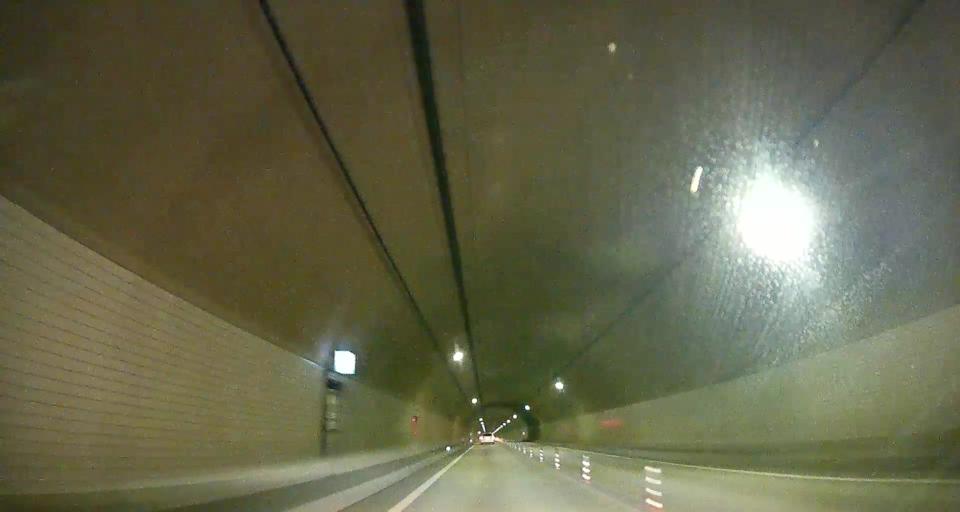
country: JP
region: Iwate
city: Miyako
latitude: 39.9304
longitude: 141.8624
